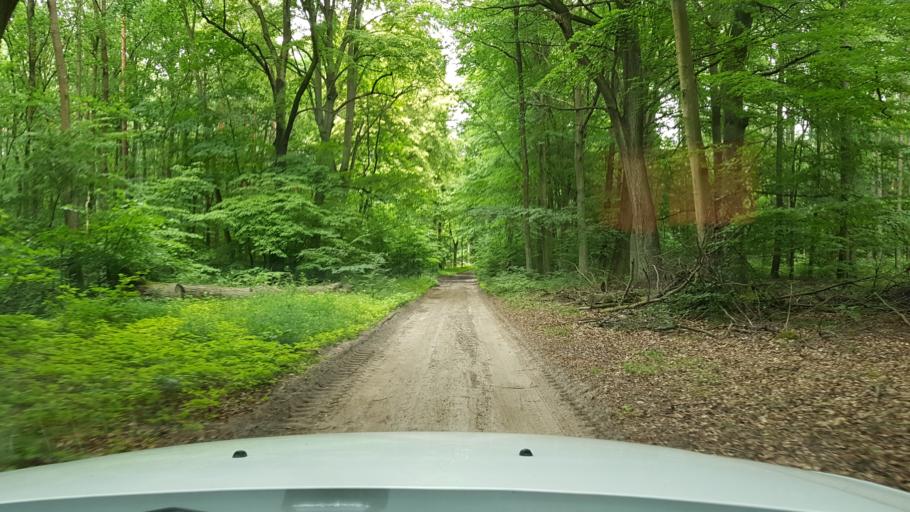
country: PL
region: West Pomeranian Voivodeship
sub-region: Powiat mysliborski
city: Boleszkowice
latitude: 52.6672
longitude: 14.5830
